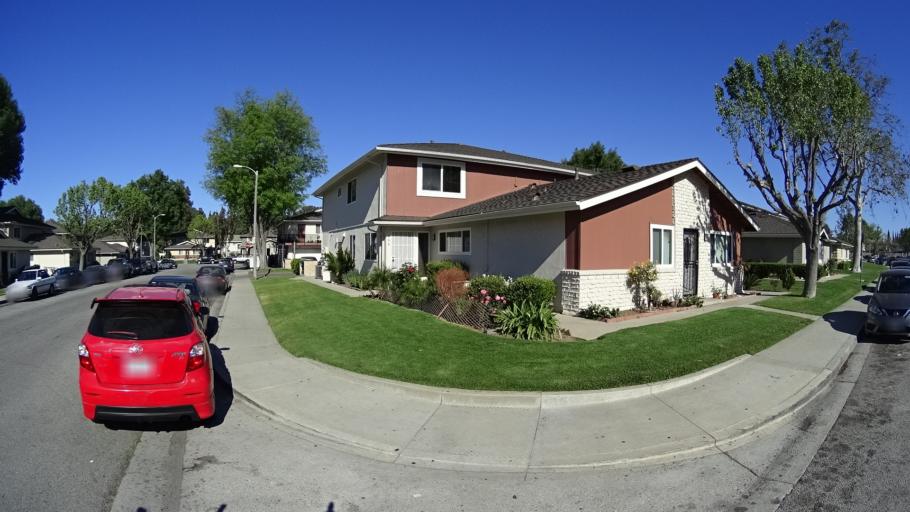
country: US
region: California
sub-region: Ventura County
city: Casa Conejo
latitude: 34.1865
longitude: -118.9153
